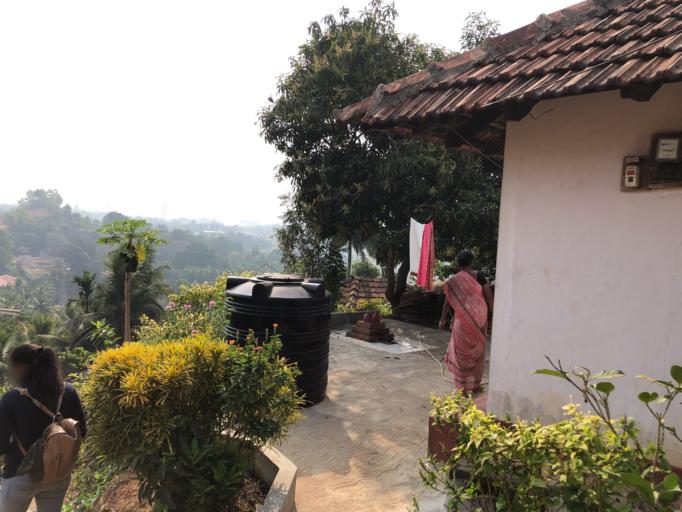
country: IN
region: Karnataka
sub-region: Dakshina Kannada
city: Mangalore
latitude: 12.8731
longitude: 74.8948
